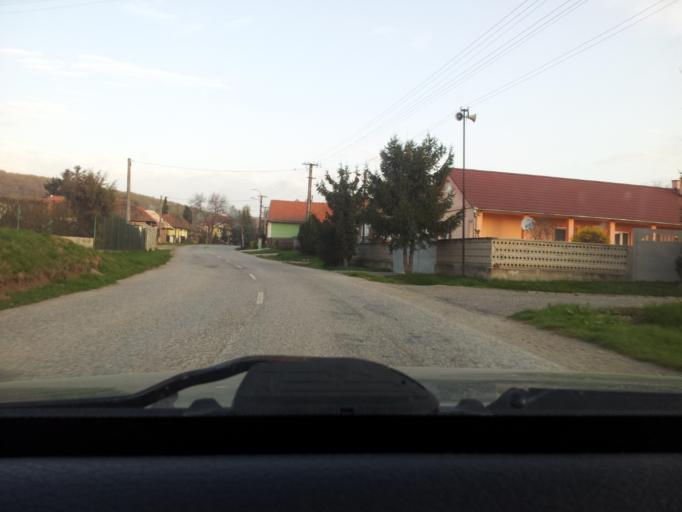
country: SK
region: Nitriansky
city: Tlmace
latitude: 48.2739
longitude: 18.5075
